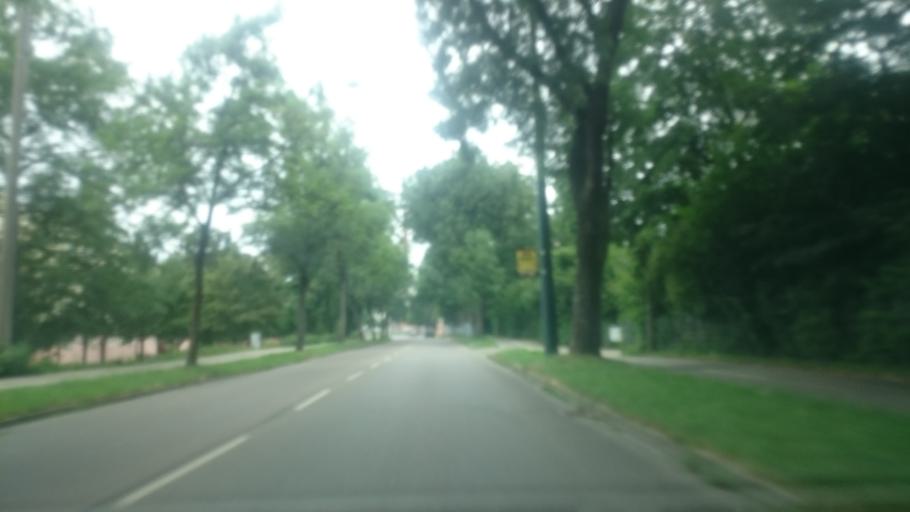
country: DE
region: Bavaria
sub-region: Swabia
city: Augsburg
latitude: 48.3613
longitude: 10.9312
